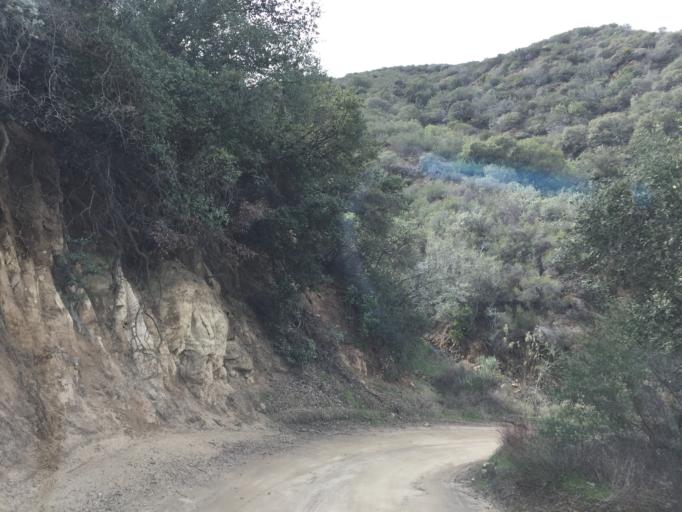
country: US
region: California
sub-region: San Bernardino County
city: Yucaipa
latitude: 34.1081
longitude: -117.0288
